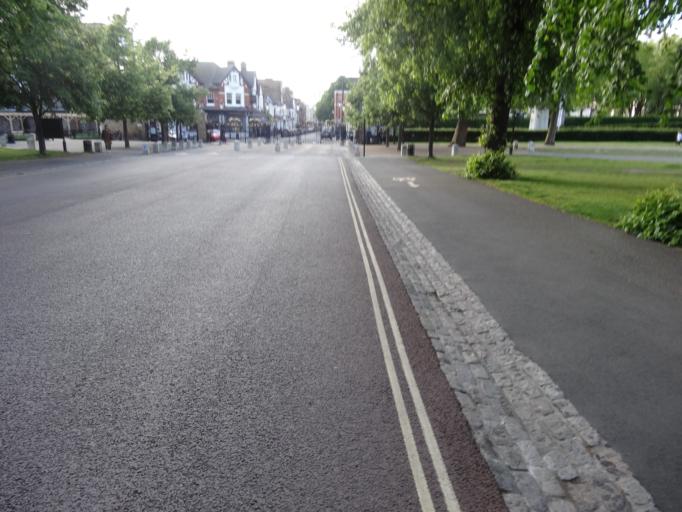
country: GB
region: England
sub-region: Greater London
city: Blackheath
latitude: 51.4793
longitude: -0.0064
